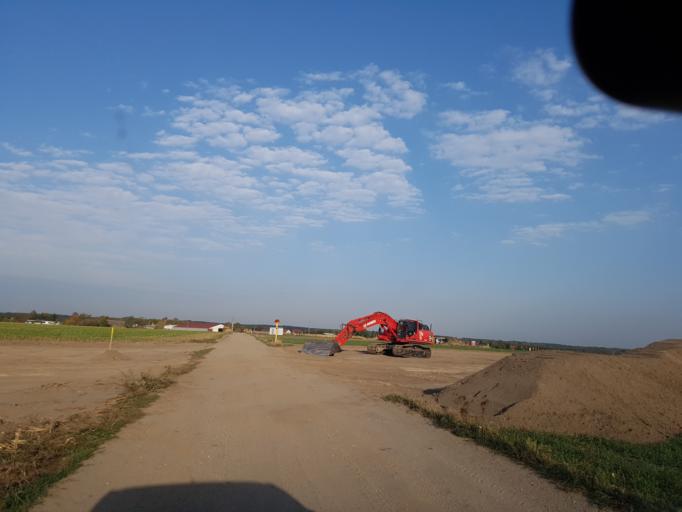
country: DE
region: Brandenburg
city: Finsterwalde
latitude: 51.5998
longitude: 13.6790
